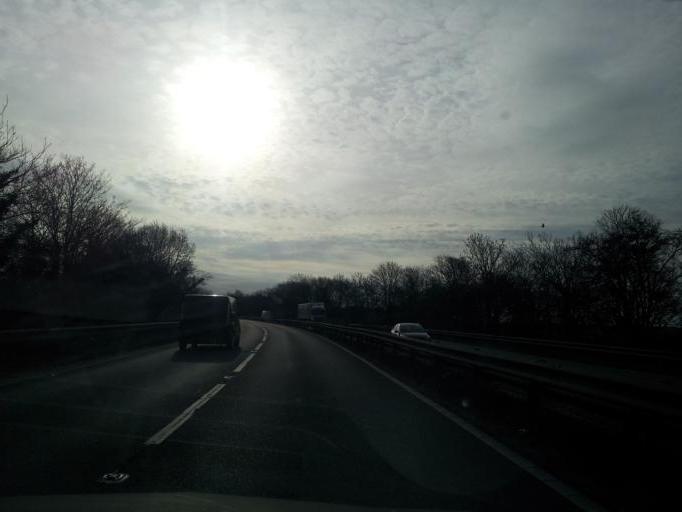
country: GB
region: England
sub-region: Peterborough
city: Wansford
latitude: 52.5682
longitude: -0.3934
